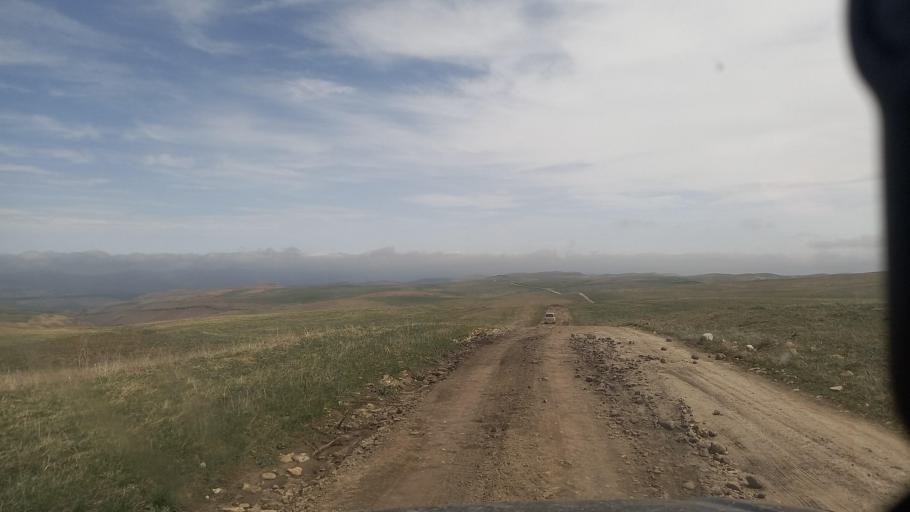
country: RU
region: Stavropol'skiy
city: Kislovodsk
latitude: 43.7583
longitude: 42.7762
